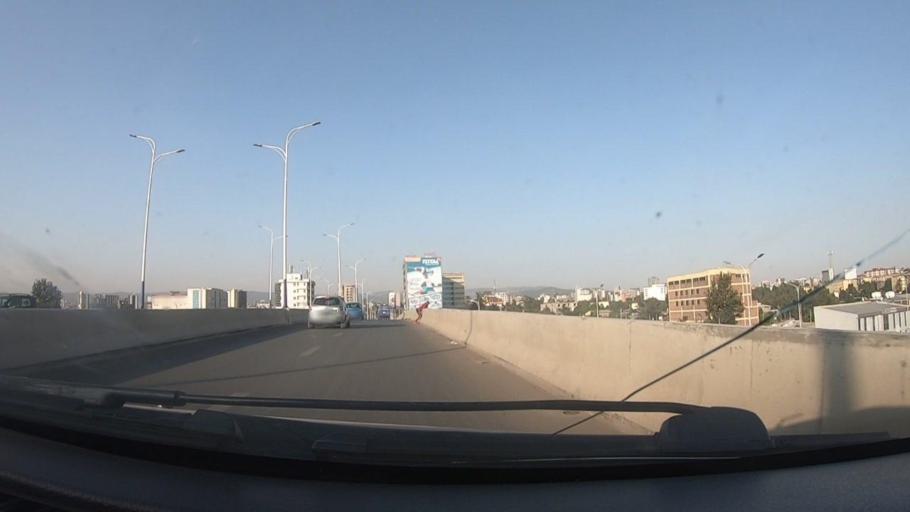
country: ET
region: Adis Abeba
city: Addis Ababa
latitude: 8.9844
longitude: 38.7503
